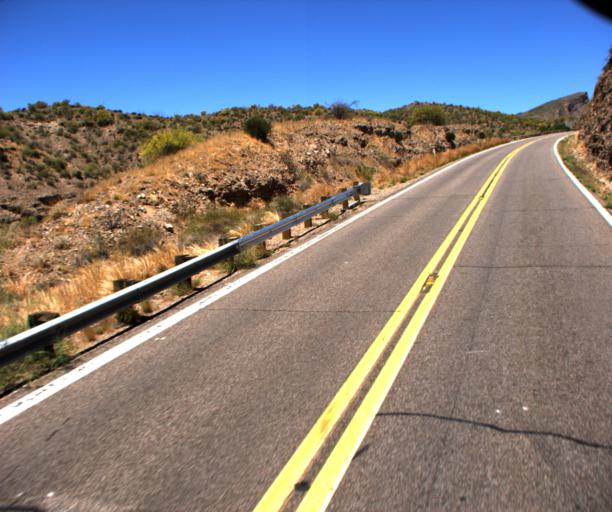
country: US
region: Arizona
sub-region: Pinal County
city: Kearny
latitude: 33.1613
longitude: -110.8047
